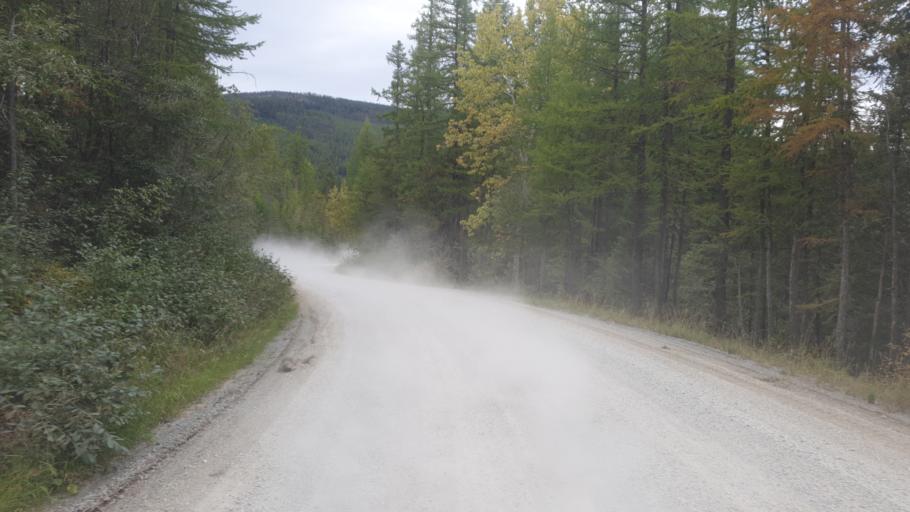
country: US
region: Montana
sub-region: Flathead County
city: Lakeside
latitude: 47.9914
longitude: -114.3265
